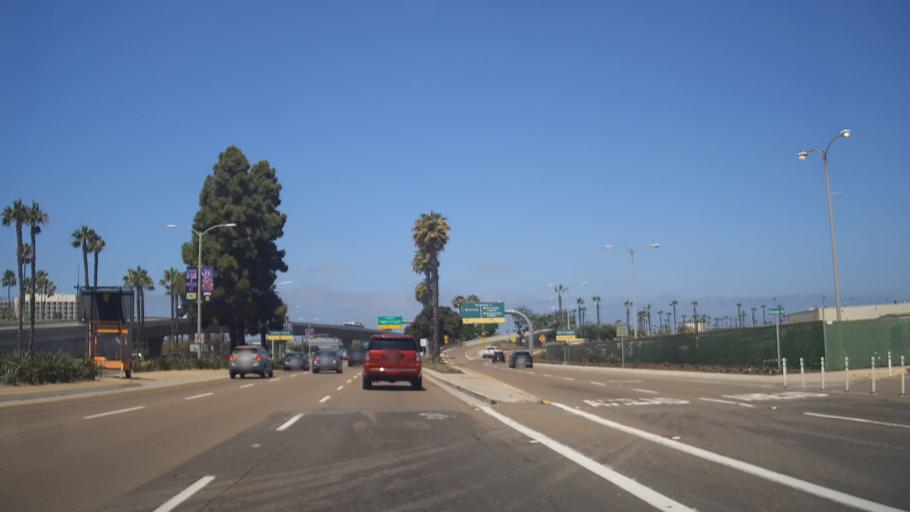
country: US
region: California
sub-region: San Diego County
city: San Diego
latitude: 32.7280
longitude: -117.1873
